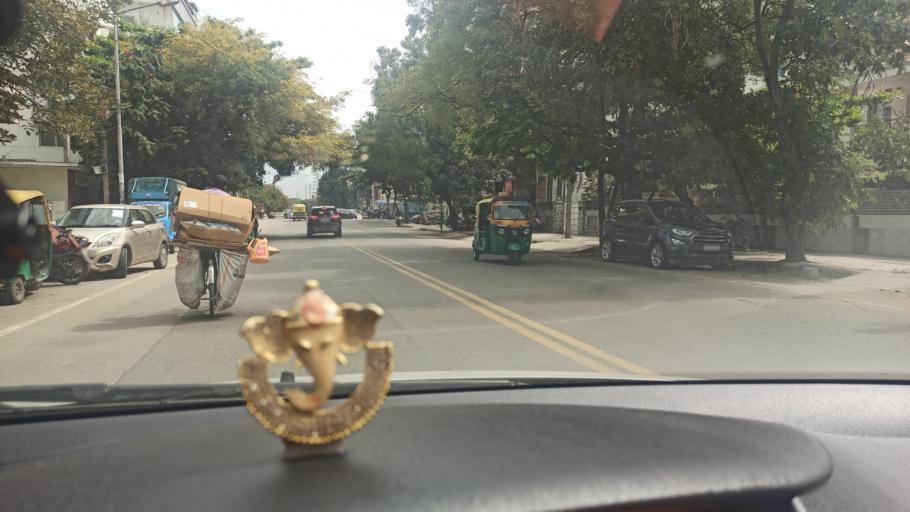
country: IN
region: Karnataka
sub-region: Bangalore Urban
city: Bangalore
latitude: 12.9124
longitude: 77.6343
